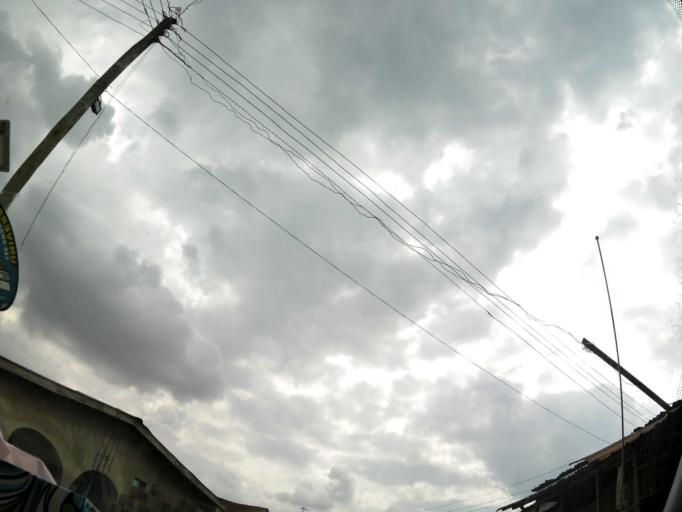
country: NG
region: Oyo
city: Ibadan
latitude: 7.4328
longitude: 3.9399
